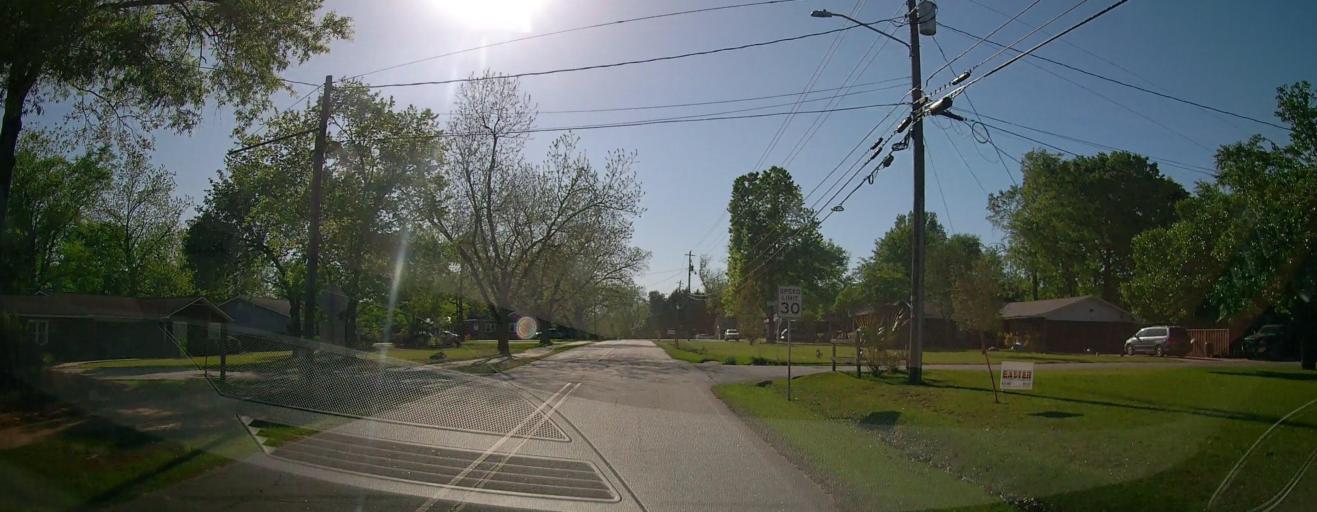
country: US
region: Georgia
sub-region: Houston County
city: Perry
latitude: 32.4506
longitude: -83.7106
